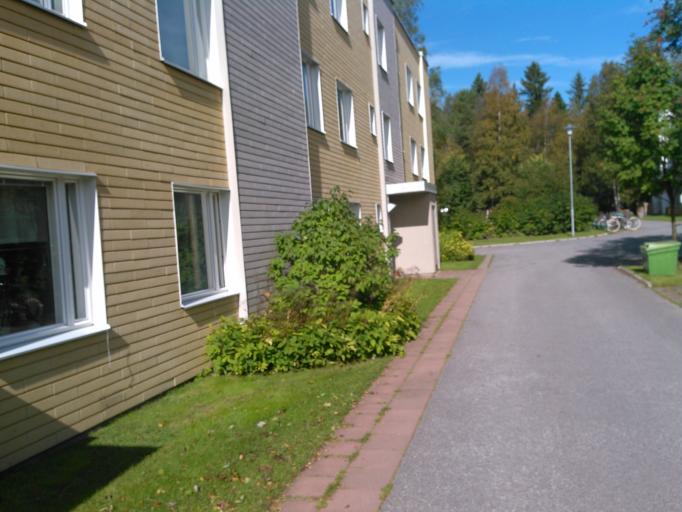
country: SE
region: Vaesterbotten
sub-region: Umea Kommun
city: Umea
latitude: 63.8005
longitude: 20.3240
